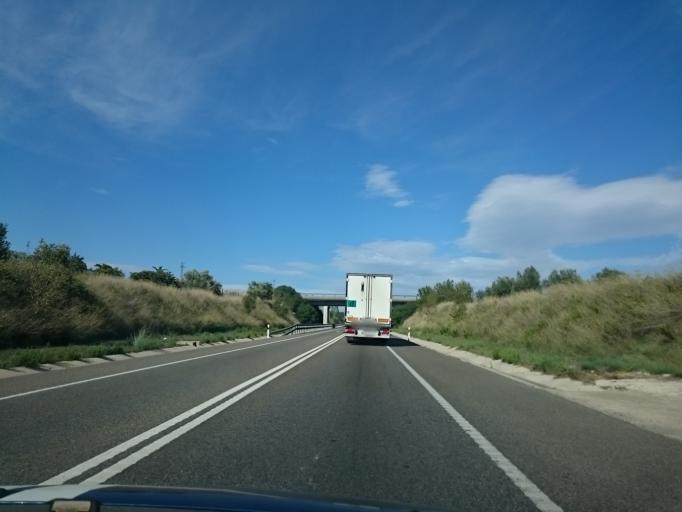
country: ES
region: Catalonia
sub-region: Provincia de Barcelona
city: Vilafranca del Penedes
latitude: 41.3420
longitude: 1.7104
